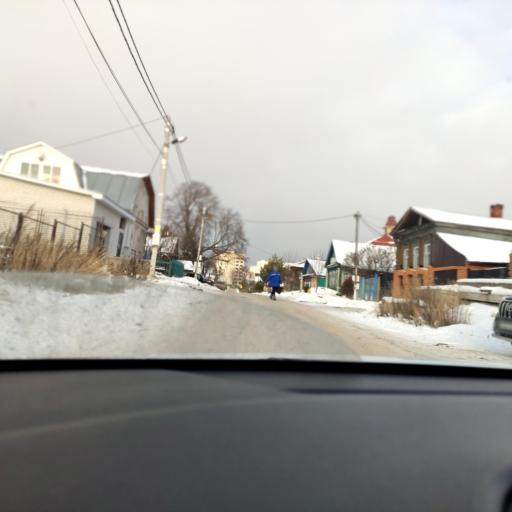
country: RU
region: Tatarstan
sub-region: Gorod Kazan'
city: Kazan
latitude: 55.7926
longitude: 49.0596
